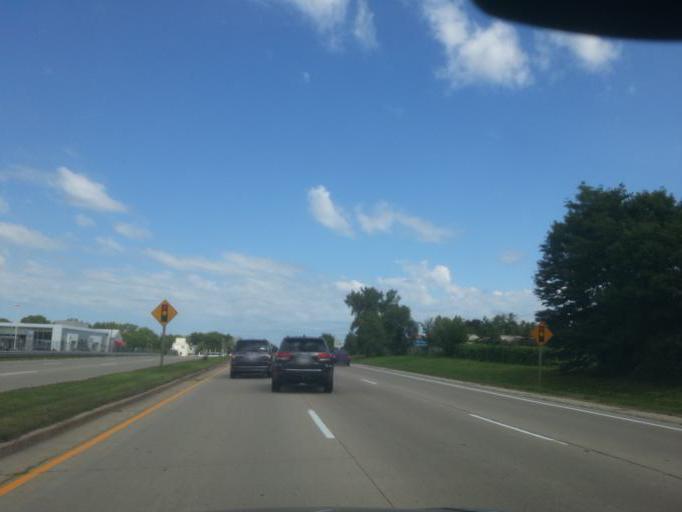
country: US
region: Wisconsin
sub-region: Dane County
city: Monona
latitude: 43.1143
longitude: -89.3220
